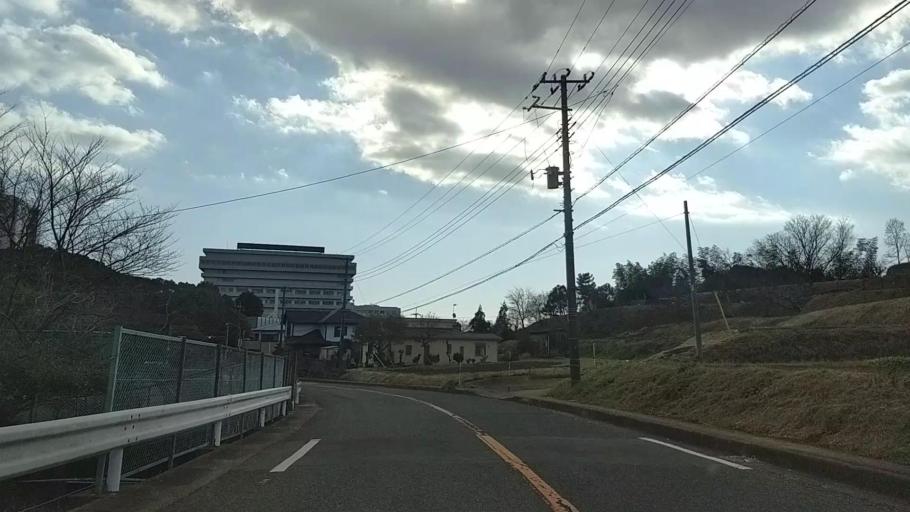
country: JP
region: Kanagawa
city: Isehara
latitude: 35.4101
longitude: 139.3133
